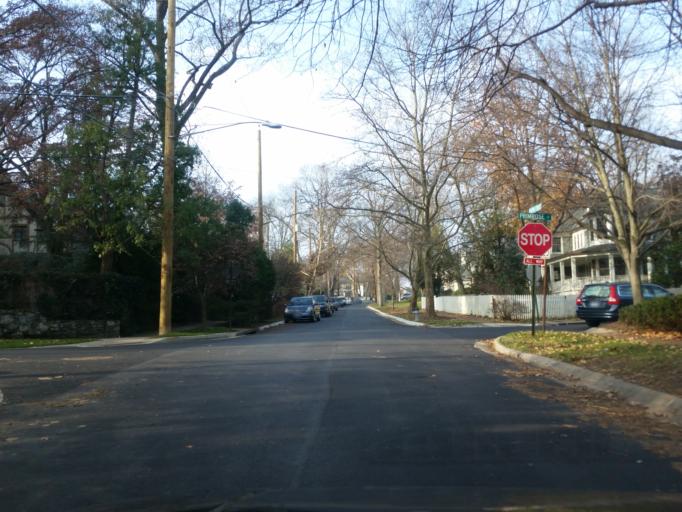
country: US
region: Maryland
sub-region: Montgomery County
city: Chevy Chase
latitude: 38.9743
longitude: -77.0706
